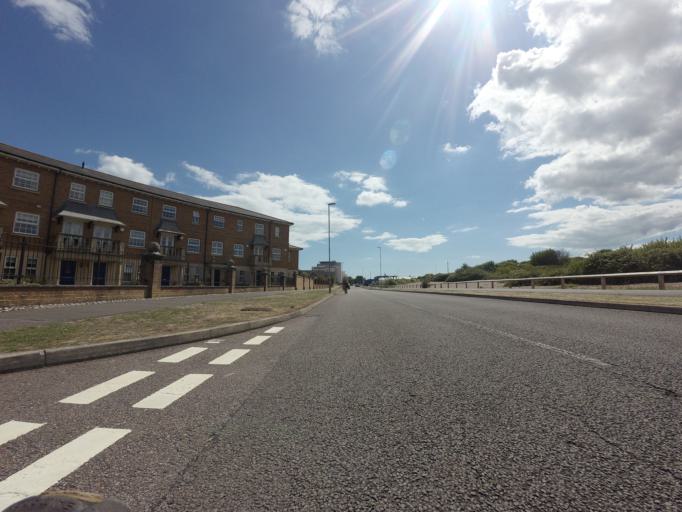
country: GB
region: England
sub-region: East Sussex
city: Pevensey
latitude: 50.7976
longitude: 0.3280
